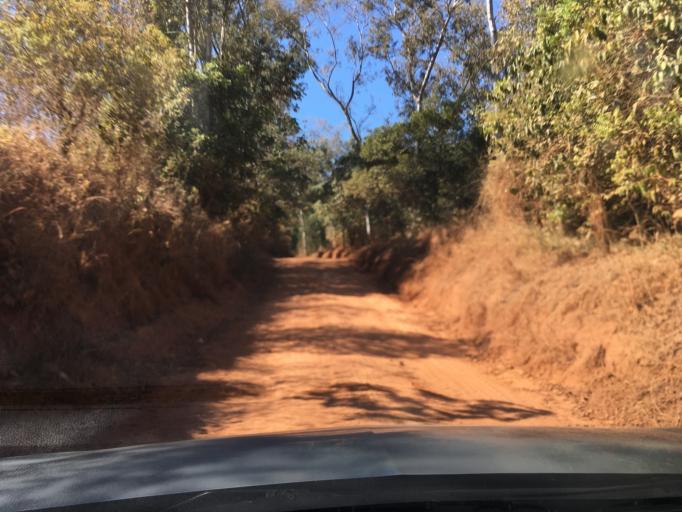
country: BR
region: Minas Gerais
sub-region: Campestre
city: Campestre
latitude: -21.5798
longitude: -46.2041
